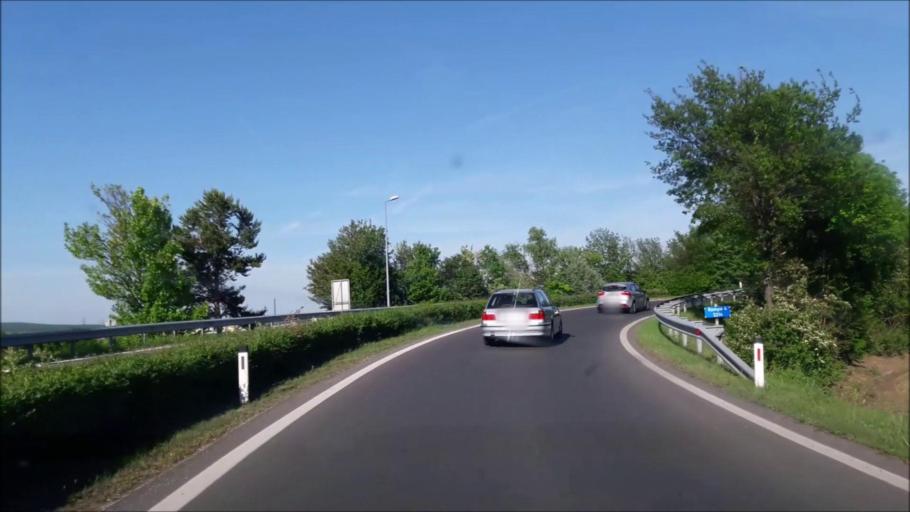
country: AT
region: Burgenland
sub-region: Eisenstadt Stadt
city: Eisenstadt
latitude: 47.8255
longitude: 16.5343
